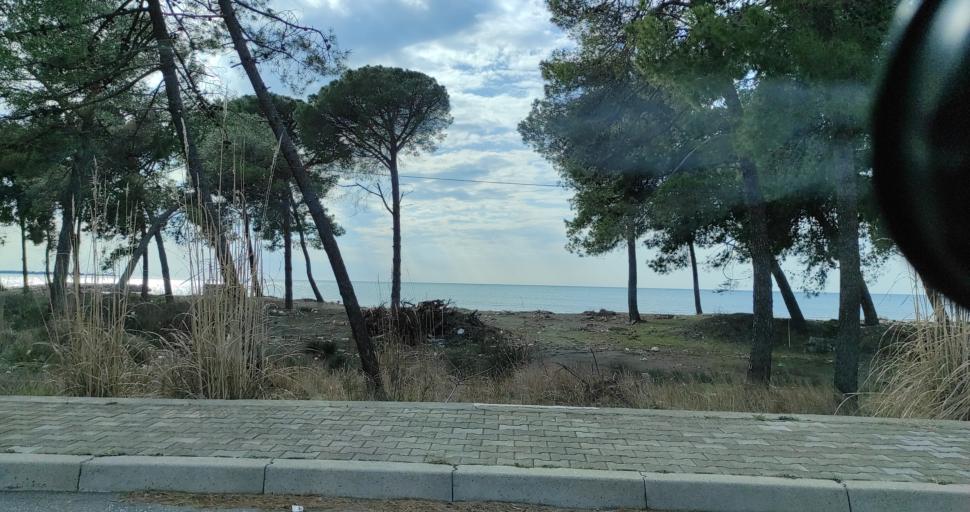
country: AL
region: Lezhe
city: Shengjin
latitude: 41.7871
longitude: 19.6034
